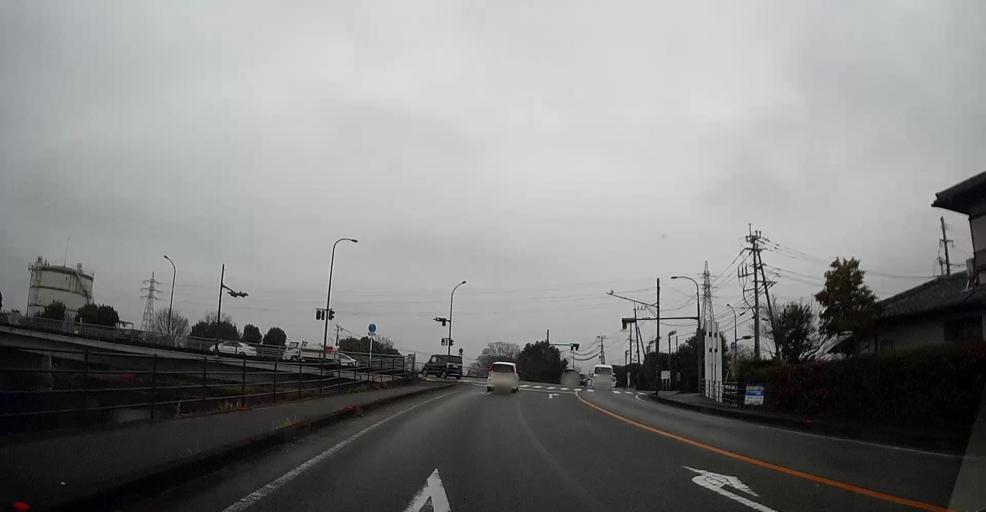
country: JP
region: Kumamoto
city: Kumamoto
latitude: 32.7646
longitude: 130.7525
